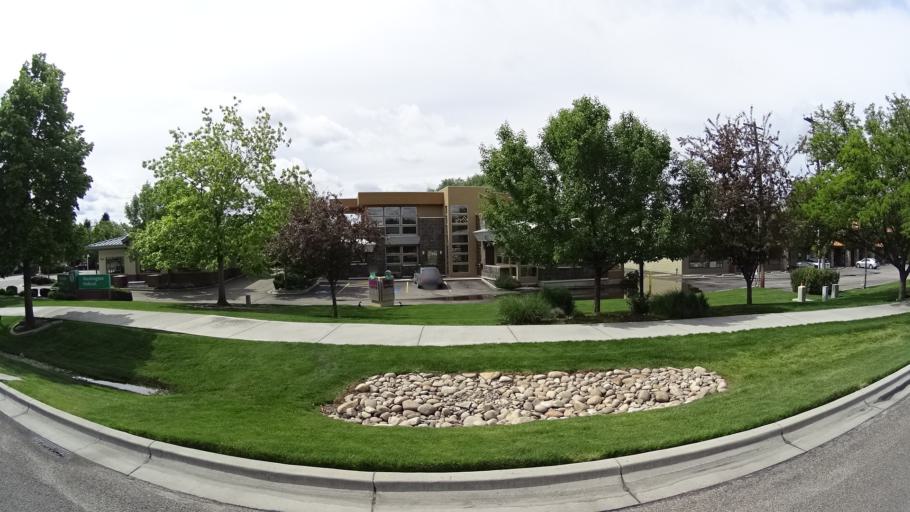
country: US
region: Idaho
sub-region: Ada County
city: Eagle
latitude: 43.6946
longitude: -116.3457
